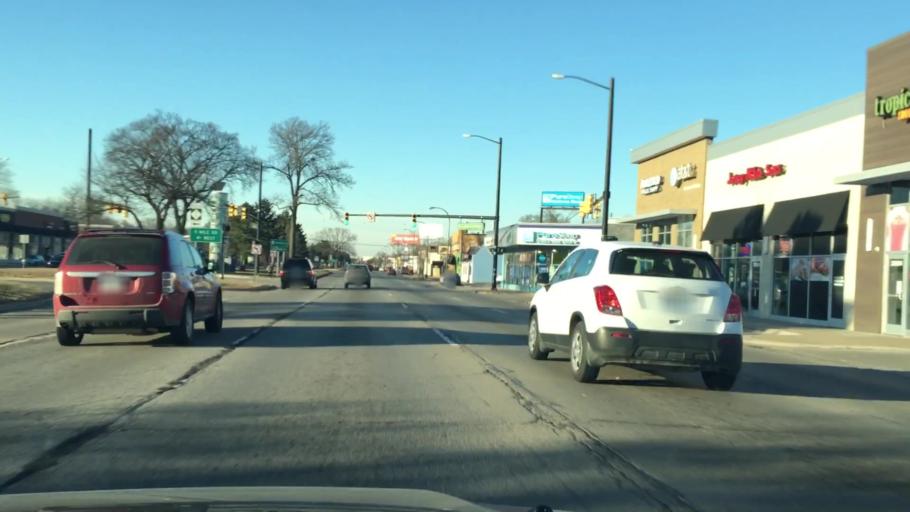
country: US
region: Michigan
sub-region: Oakland County
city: Ferndale
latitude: 42.4629
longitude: -83.1359
